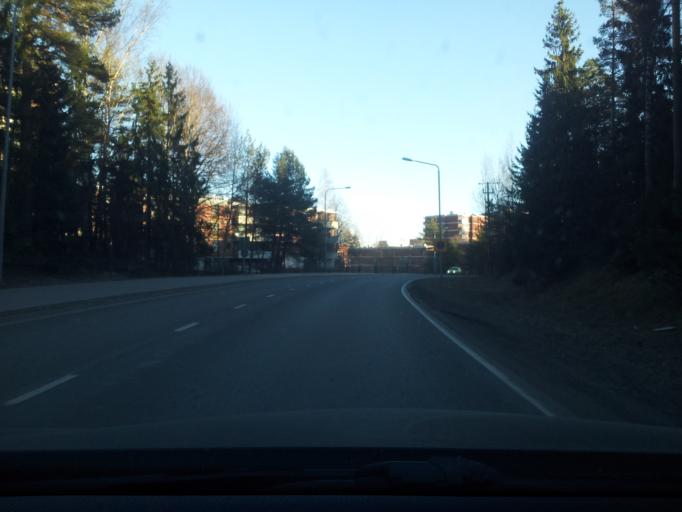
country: FI
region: Uusimaa
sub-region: Helsinki
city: Kauniainen
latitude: 60.1748
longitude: 24.7206
